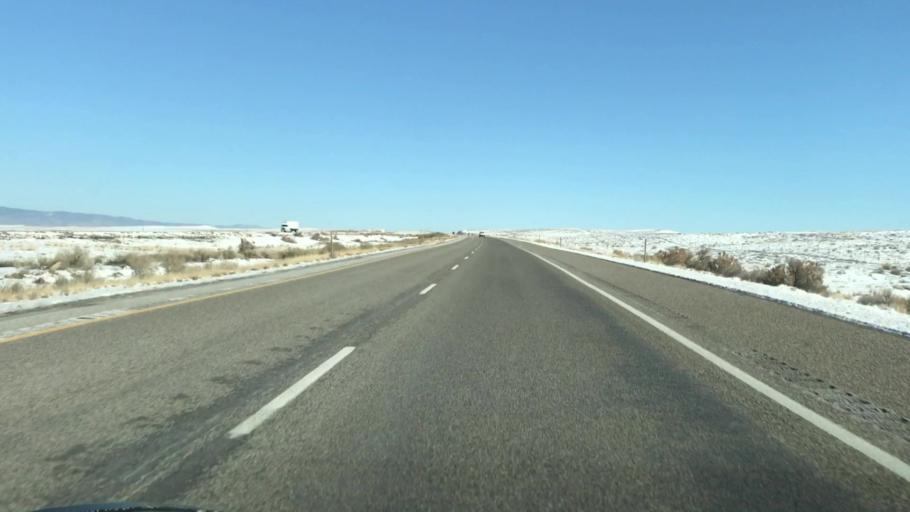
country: US
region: Colorado
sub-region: Mesa County
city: Loma
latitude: 39.1330
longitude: -109.1597
